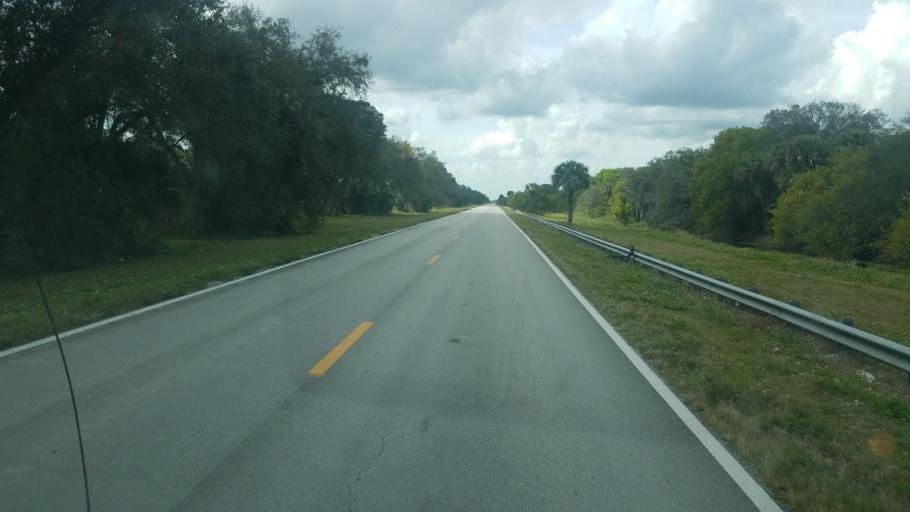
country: US
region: Florida
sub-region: Indian River County
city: West Vero Corridor
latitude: 27.4484
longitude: -80.6355
